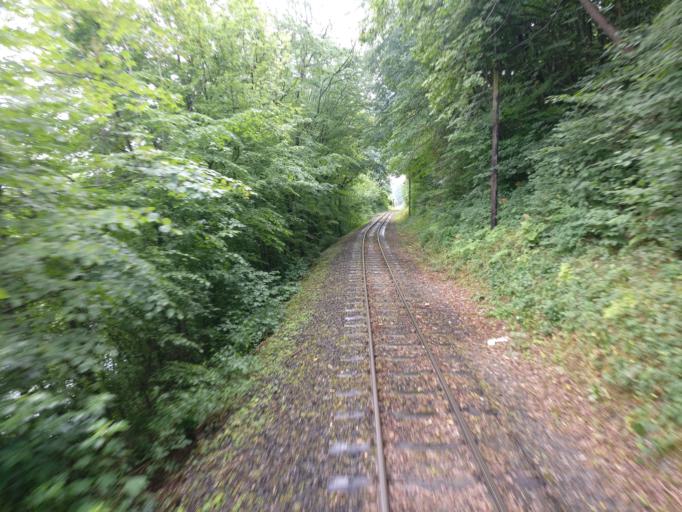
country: AT
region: Upper Austria
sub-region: Politischer Bezirk Steyr-Land
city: Garsten
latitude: 48.0398
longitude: 14.4036
